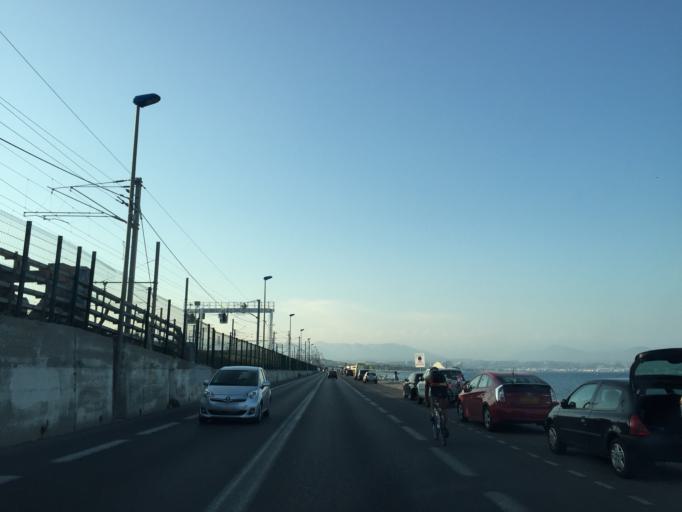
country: FR
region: Provence-Alpes-Cote d'Azur
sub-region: Departement des Alpes-Maritimes
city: Antibes
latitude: 43.5968
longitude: 7.1254
